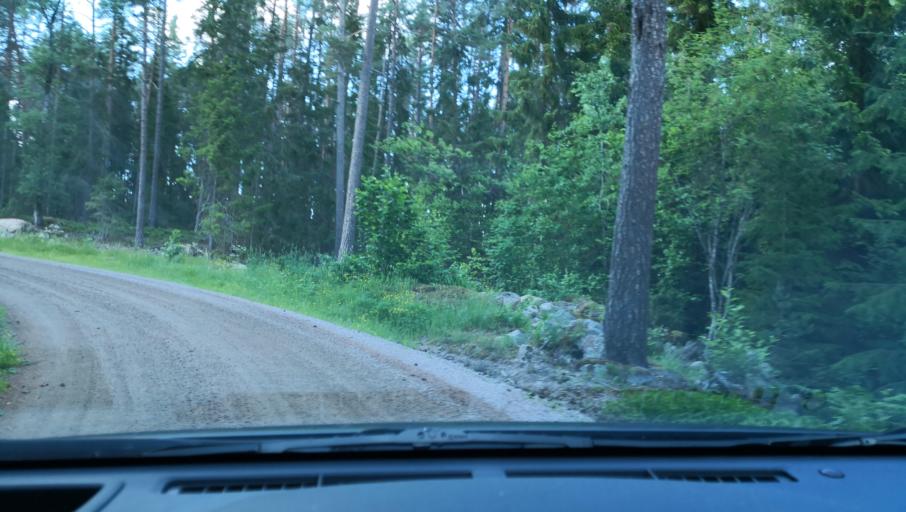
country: SE
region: Uppsala
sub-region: Enkopings Kommun
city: Orsundsbro
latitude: 59.8362
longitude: 17.2261
